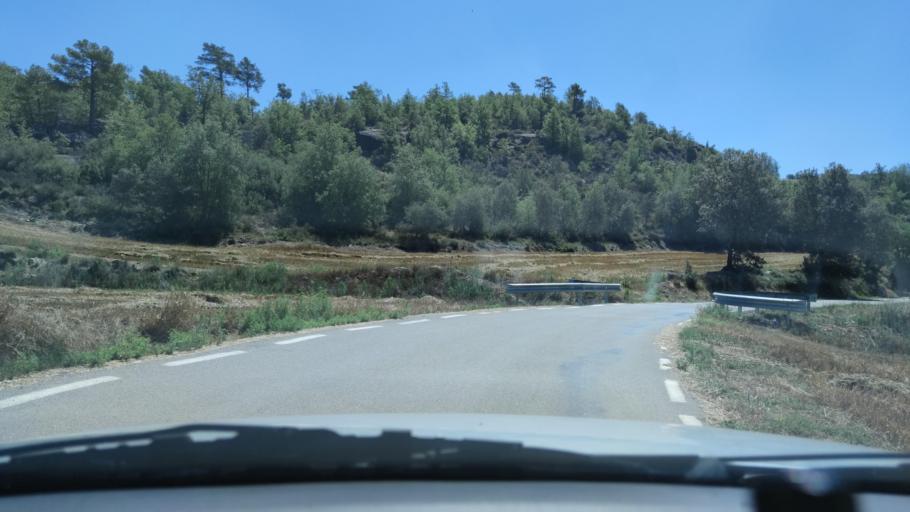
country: ES
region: Catalonia
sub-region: Provincia de Lleida
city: Tora de Riubregos
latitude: 41.8316
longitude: 1.4230
